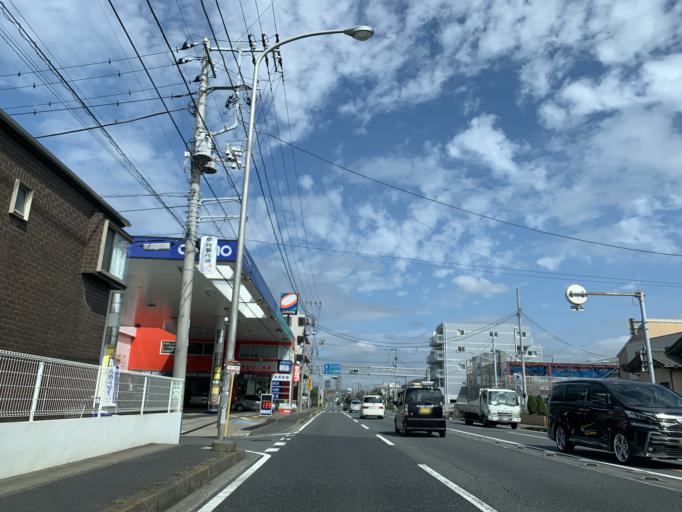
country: JP
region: Tokyo
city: Urayasu
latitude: 35.6965
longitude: 139.9236
